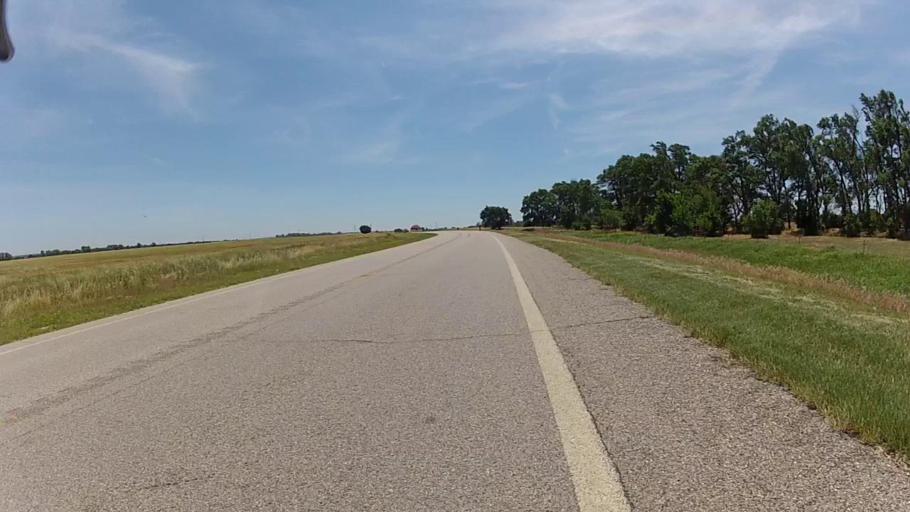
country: US
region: Kansas
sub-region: Barber County
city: Medicine Lodge
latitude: 37.2548
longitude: -98.5200
